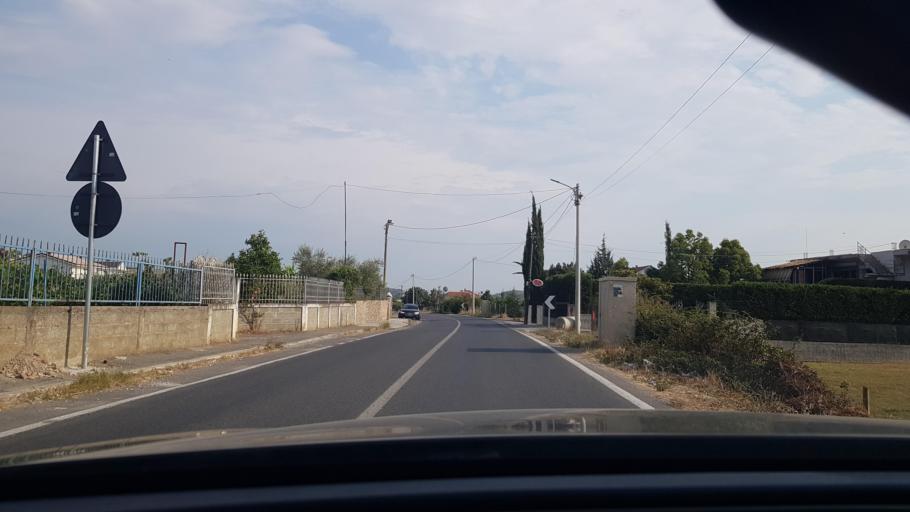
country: AL
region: Durres
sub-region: Rrethi i Durresit
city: Manze
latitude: 41.4653
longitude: 19.5625
